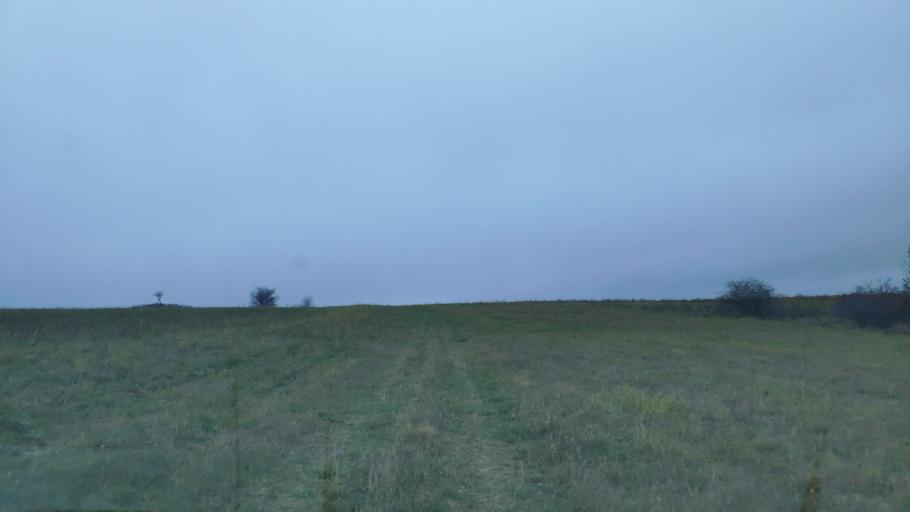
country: SK
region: Presovsky
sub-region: Okres Presov
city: Presov
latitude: 48.9329
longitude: 21.0904
